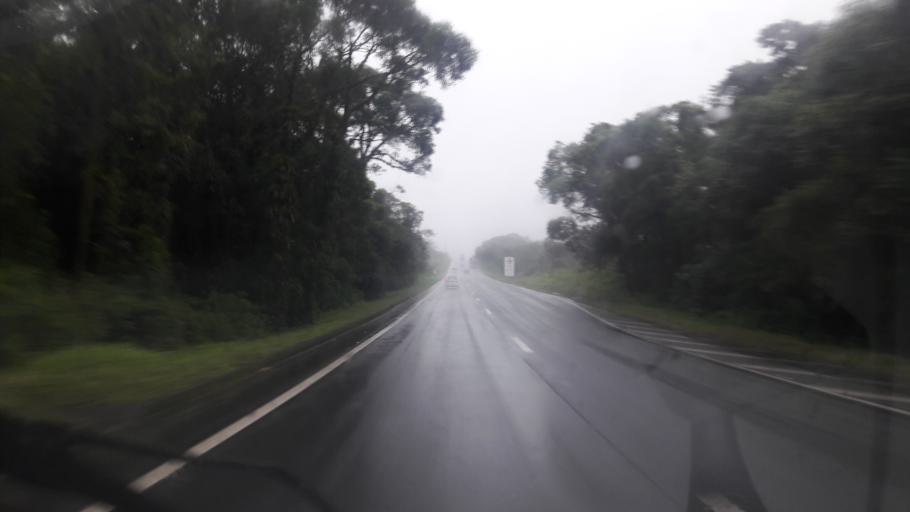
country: BR
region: Parana
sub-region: Antonina
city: Antonina
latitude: -25.1127
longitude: -48.7795
